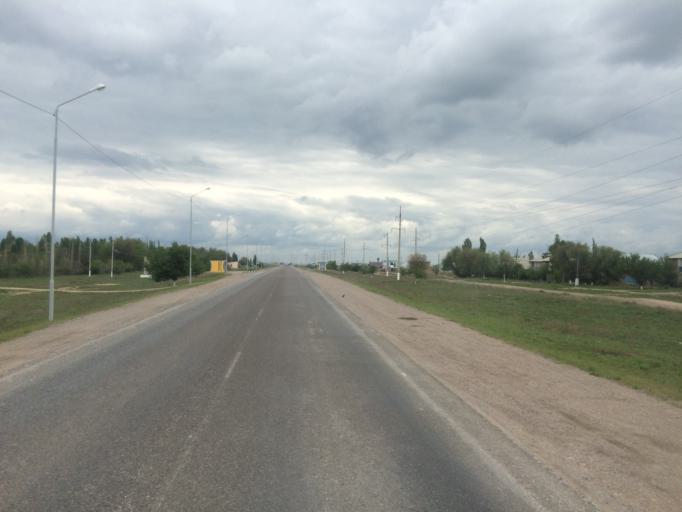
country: KG
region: Chuy
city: Sokuluk
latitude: 43.2496
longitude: 74.2907
